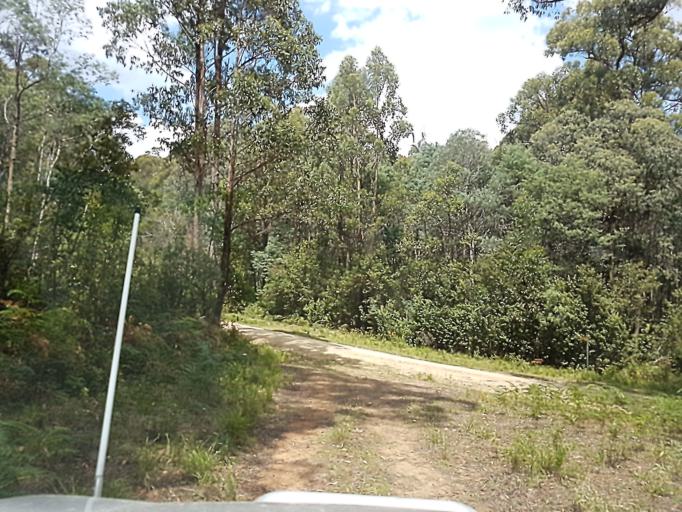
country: AU
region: Victoria
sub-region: East Gippsland
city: Lakes Entrance
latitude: -37.3315
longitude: 148.3197
